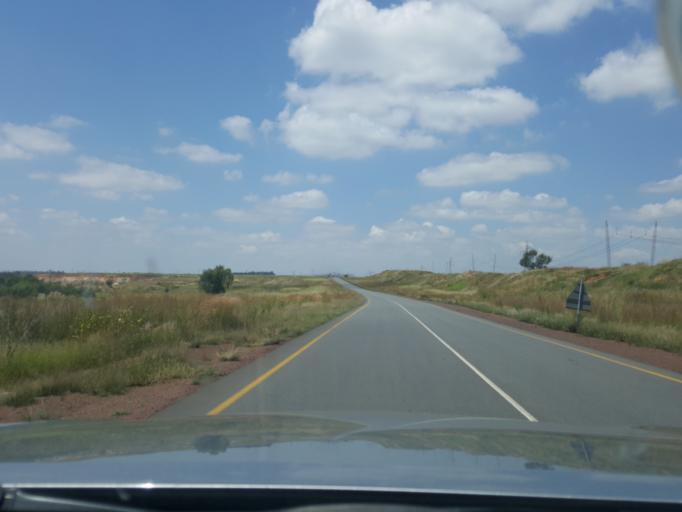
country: ZA
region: Mpumalanga
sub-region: Nkangala District Municipality
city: Witbank
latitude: -26.0149
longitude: 29.3958
